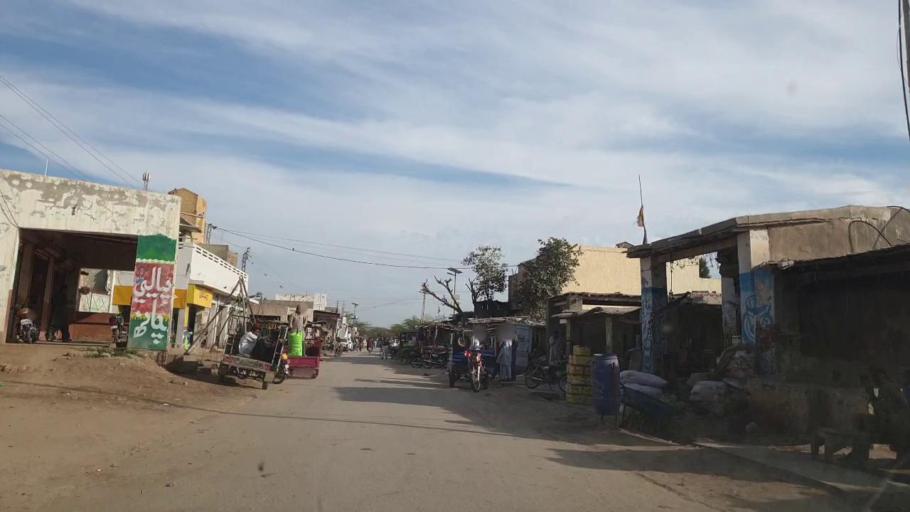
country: PK
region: Sindh
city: Pithoro
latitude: 25.6265
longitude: 69.4191
